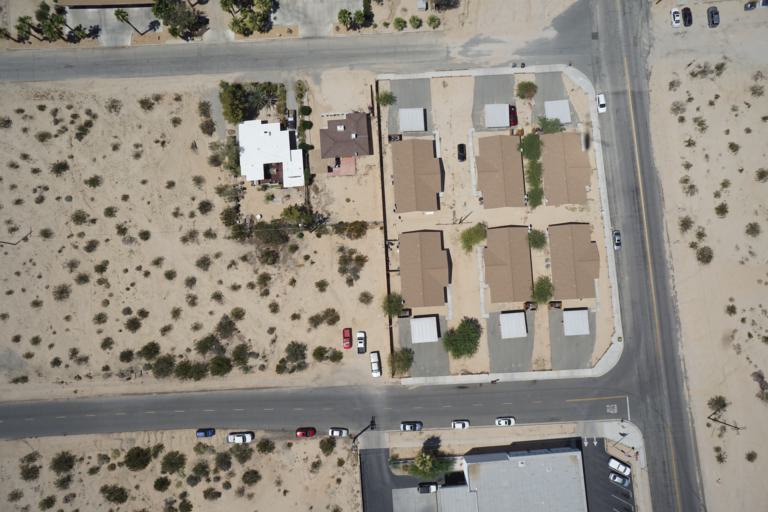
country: US
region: California
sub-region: San Bernardino County
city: Twentynine Palms
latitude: 34.1387
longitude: -116.0517
